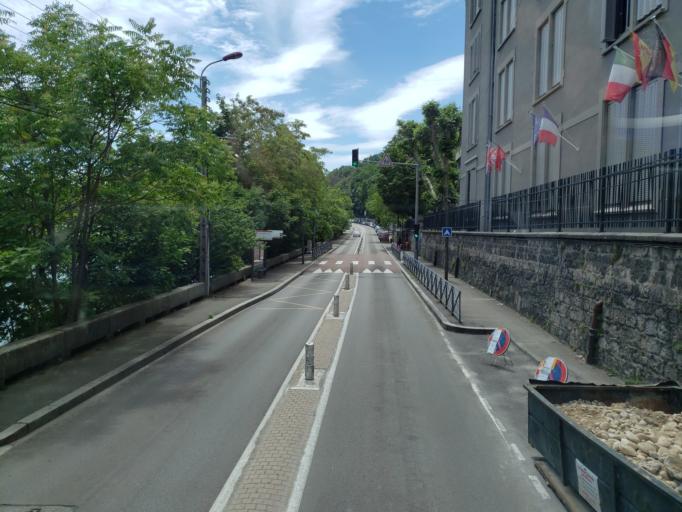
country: FR
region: Rhone-Alpes
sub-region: Departement du Rhone
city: La Mulatiere
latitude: 45.7339
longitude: 4.8127
